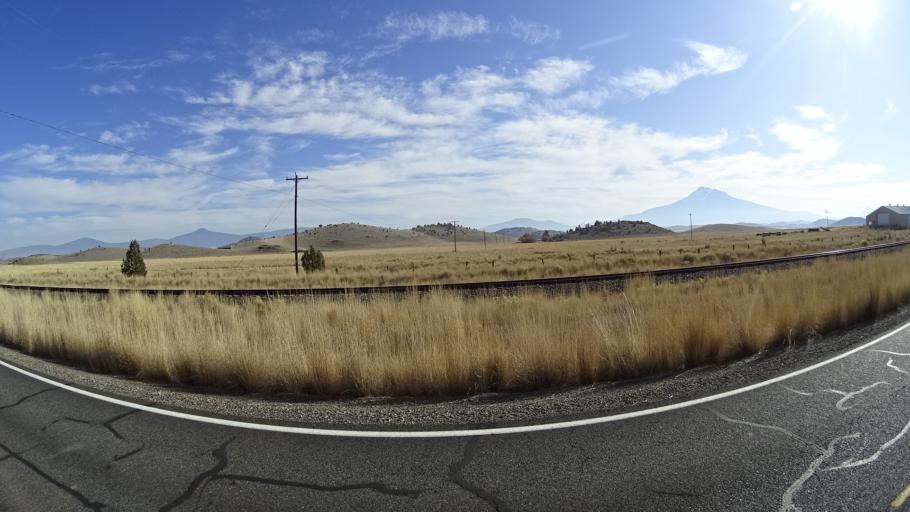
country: US
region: California
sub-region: Siskiyou County
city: Montague
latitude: 41.5846
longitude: -122.5245
